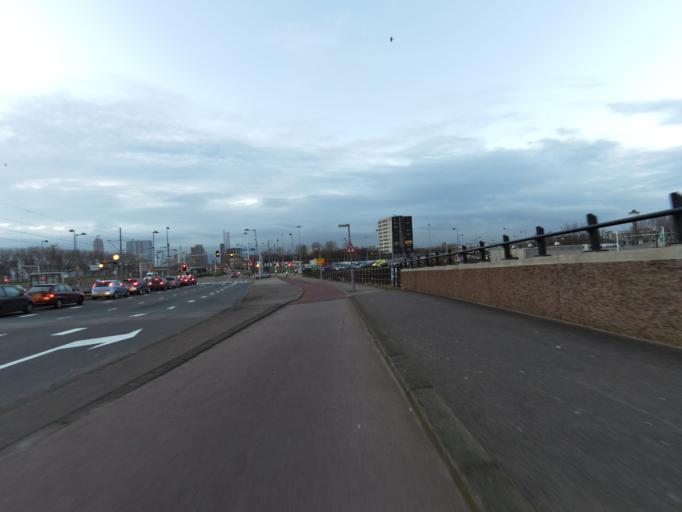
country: NL
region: South Holland
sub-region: Gemeente Rotterdam
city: Rotterdam
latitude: 51.9002
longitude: 4.5126
